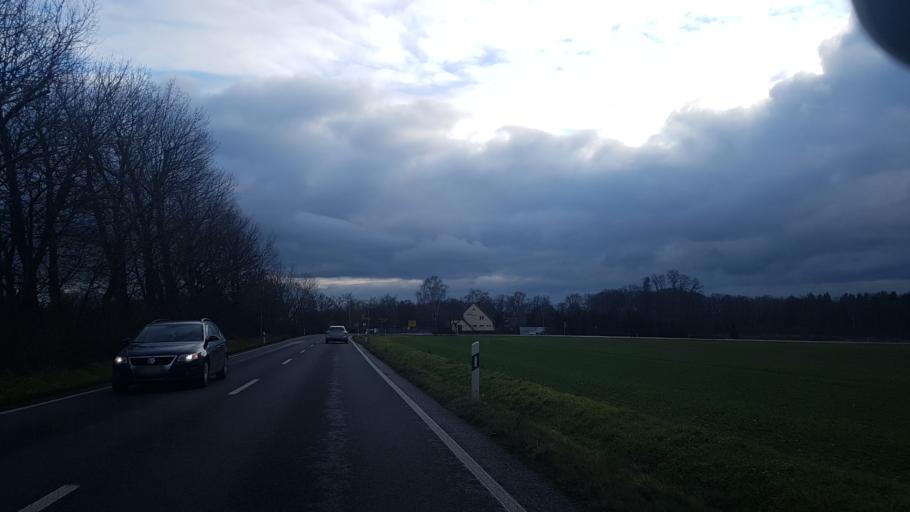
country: DE
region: Saxony
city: Zabeltitz
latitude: 51.3451
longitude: 13.5366
